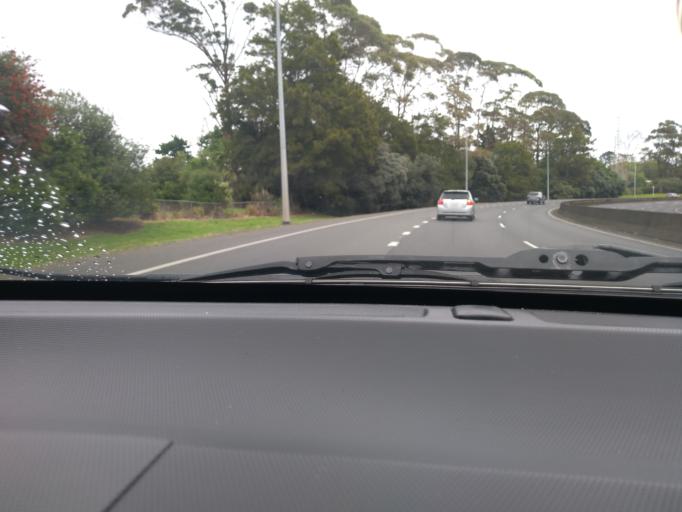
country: NZ
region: Auckland
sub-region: Auckland
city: Tamaki
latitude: -36.9166
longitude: 174.8693
